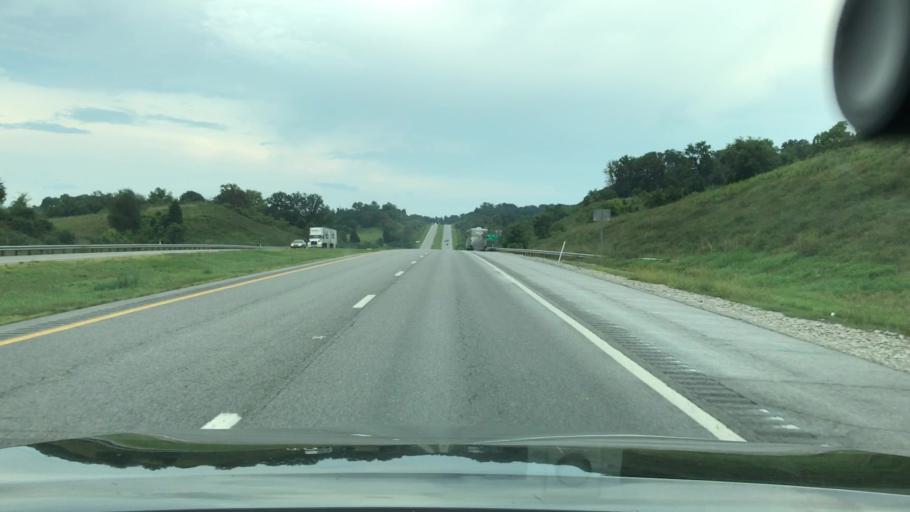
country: US
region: West Virginia
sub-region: Mason County
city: Point Pleasant
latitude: 38.8072
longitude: -82.1044
